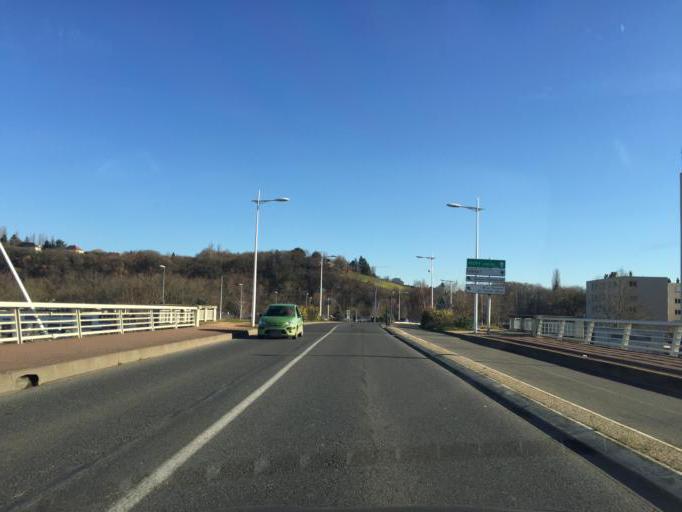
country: FR
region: Auvergne
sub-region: Departement de l'Allier
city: Vichy
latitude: 46.1420
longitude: 3.4123
